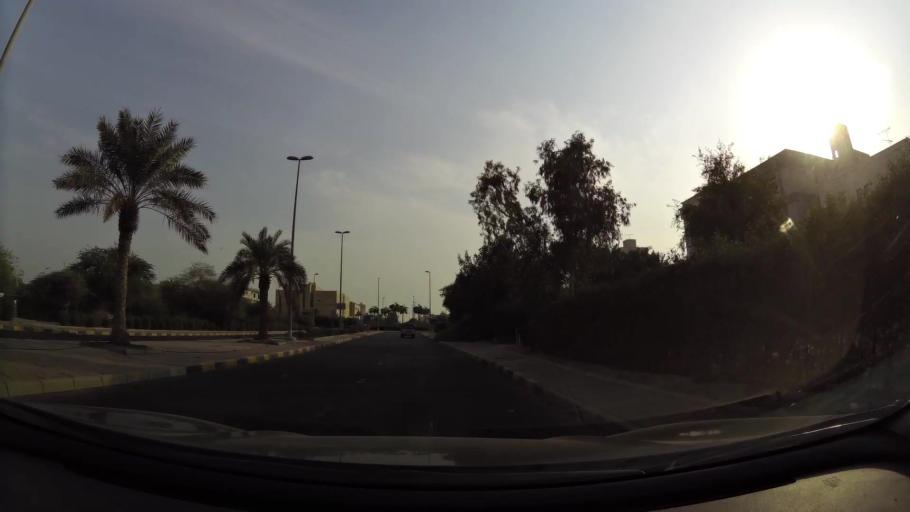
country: KW
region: Mubarak al Kabir
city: Mubarak al Kabir
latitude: 29.1995
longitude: 48.0687
